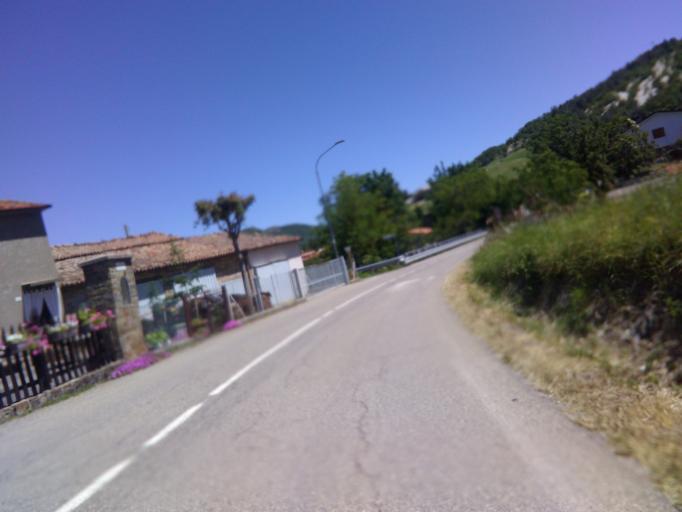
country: IT
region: Emilia-Romagna
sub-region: Provincia di Parma
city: Terenzo
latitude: 44.5766
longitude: 10.0758
